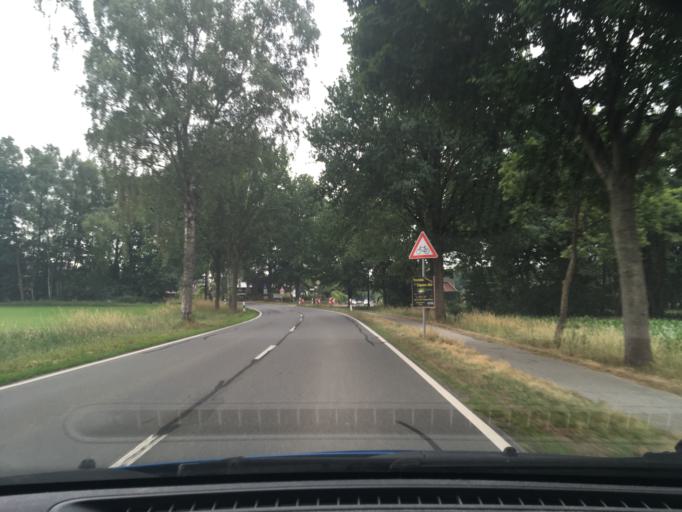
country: DE
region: Lower Saxony
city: Drestedt
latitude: 53.3368
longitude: 9.7561
